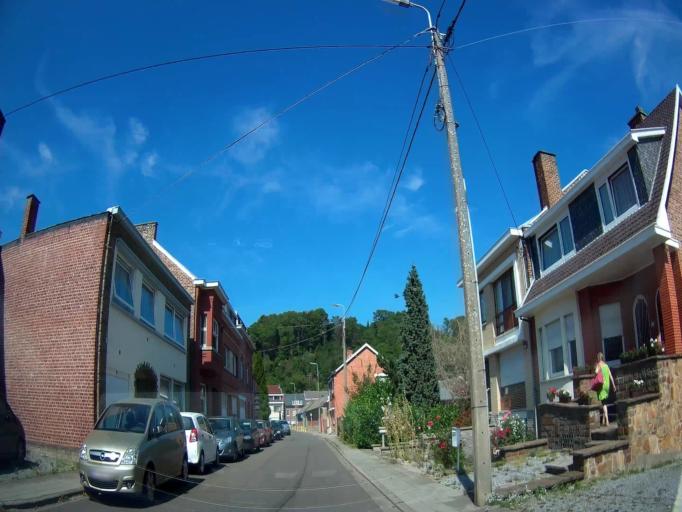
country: BE
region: Wallonia
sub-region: Province de Liege
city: Amay
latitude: 50.5484
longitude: 5.3213
